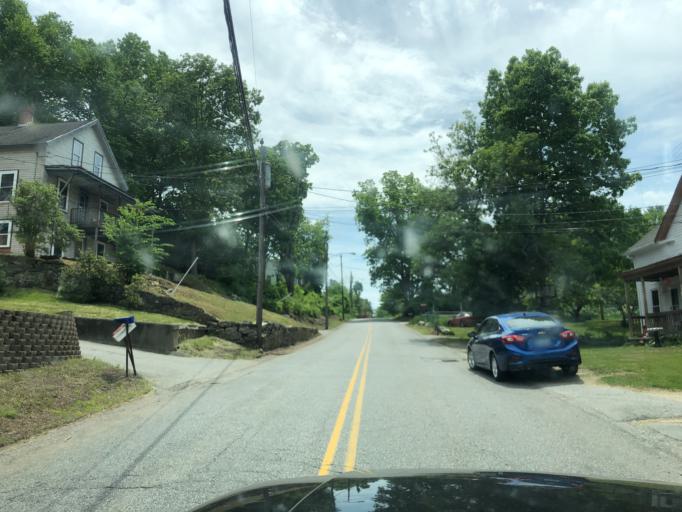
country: US
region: Connecticut
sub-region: Windham County
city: North Grosvenor Dale
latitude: 41.9867
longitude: -71.8945
